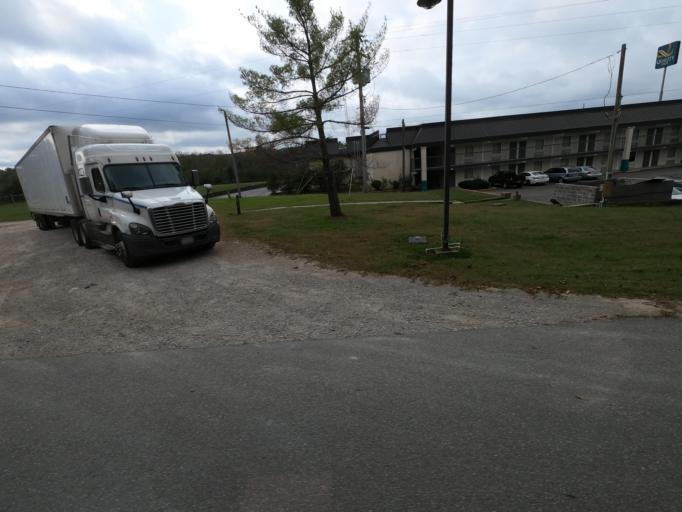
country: US
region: Tennessee
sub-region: Humphreys County
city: Waverly
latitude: 35.8821
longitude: -87.7978
